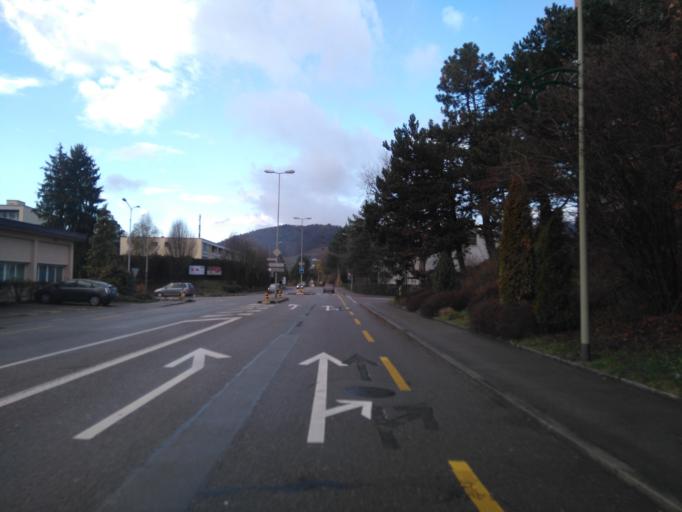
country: CH
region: Zurich
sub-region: Bezirk Dietikon
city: Unterengstringen
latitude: 47.4151
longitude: 8.4459
